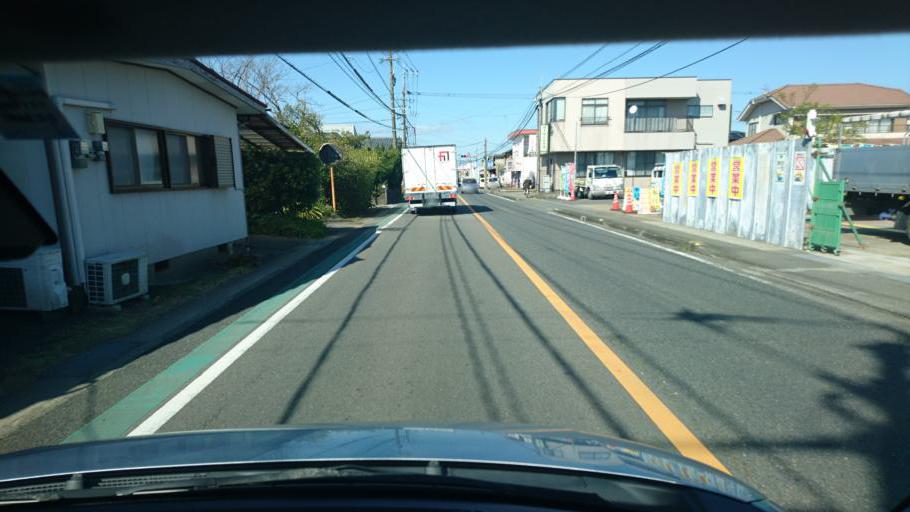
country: JP
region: Miyazaki
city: Miyazaki-shi
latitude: 31.8648
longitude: 131.4322
